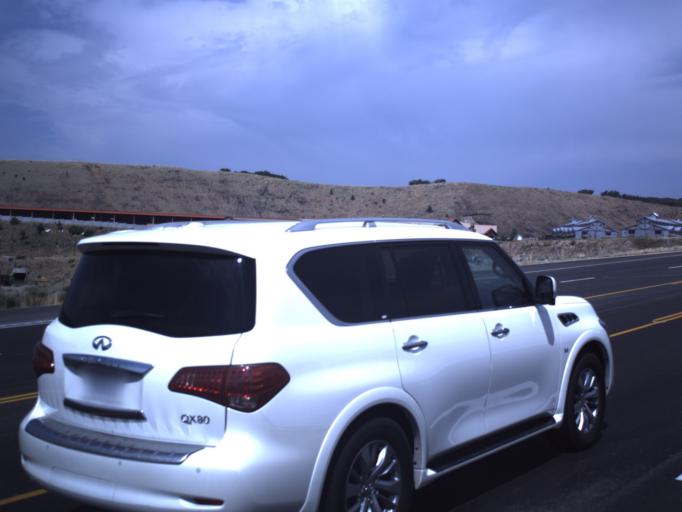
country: US
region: Utah
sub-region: Summit County
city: Park City
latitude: 40.6760
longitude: -111.4305
